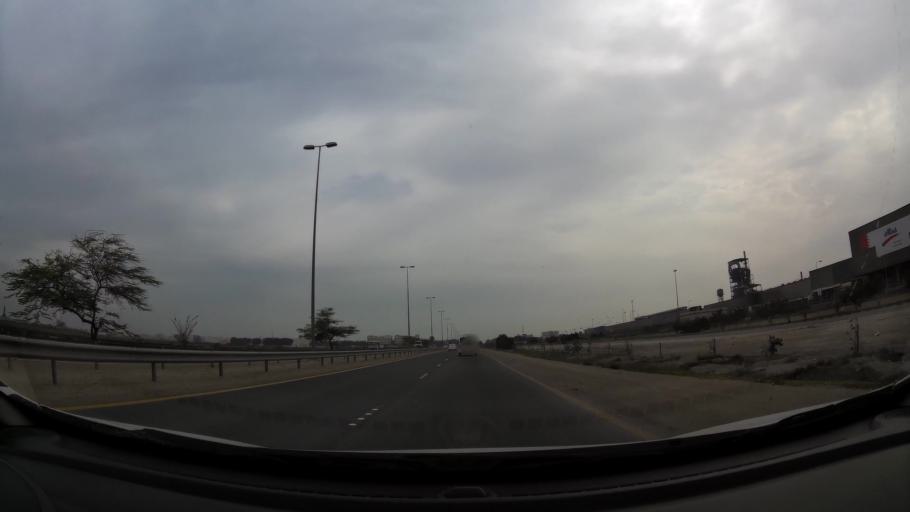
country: BH
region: Northern
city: Sitrah
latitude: 26.0911
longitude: 50.6100
